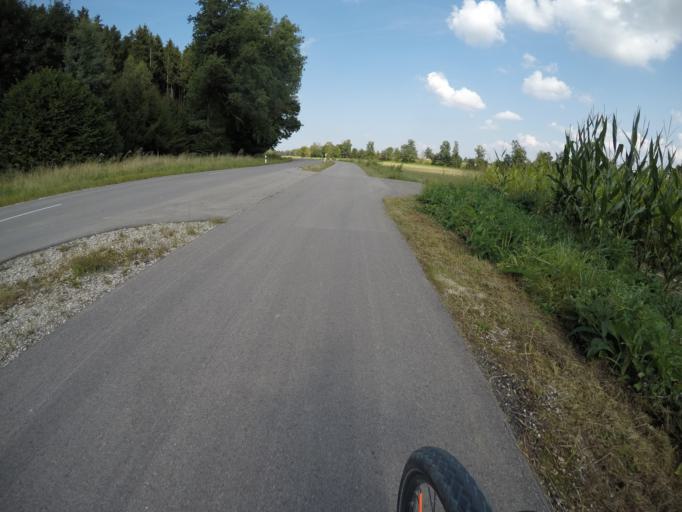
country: DE
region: Bavaria
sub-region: Swabia
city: Kuhlenthal
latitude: 48.5725
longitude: 10.8228
